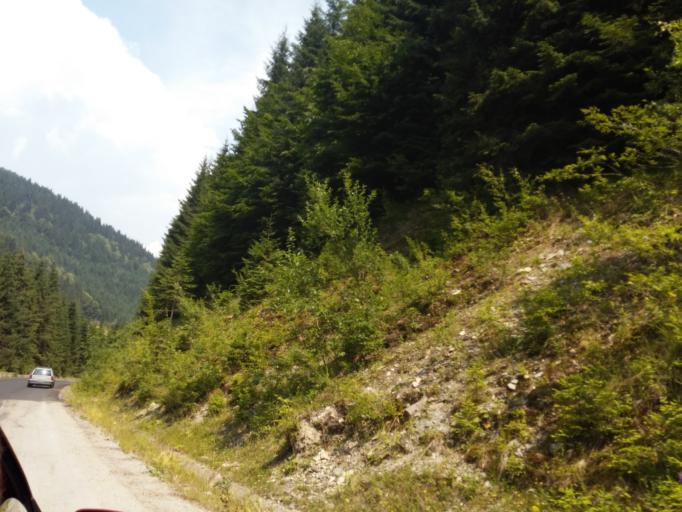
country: RO
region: Valcea
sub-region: Comuna Voineasa
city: Voineasa
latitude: 45.4288
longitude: 23.8227
